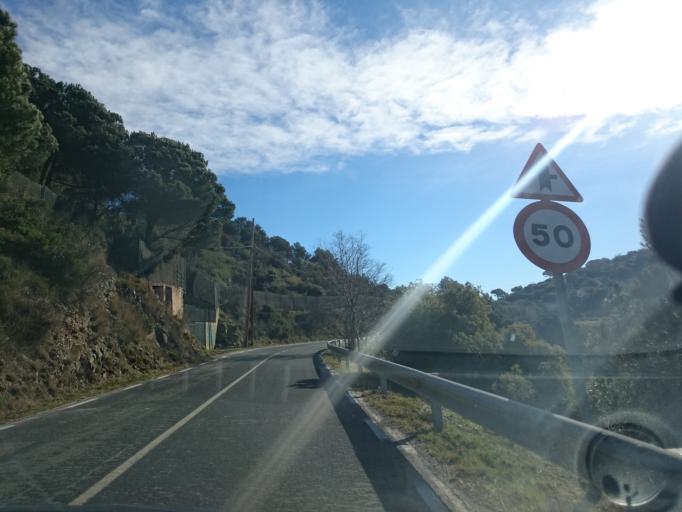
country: ES
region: Catalonia
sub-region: Provincia de Barcelona
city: Sant Just Desvern
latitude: 41.4080
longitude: 2.0995
